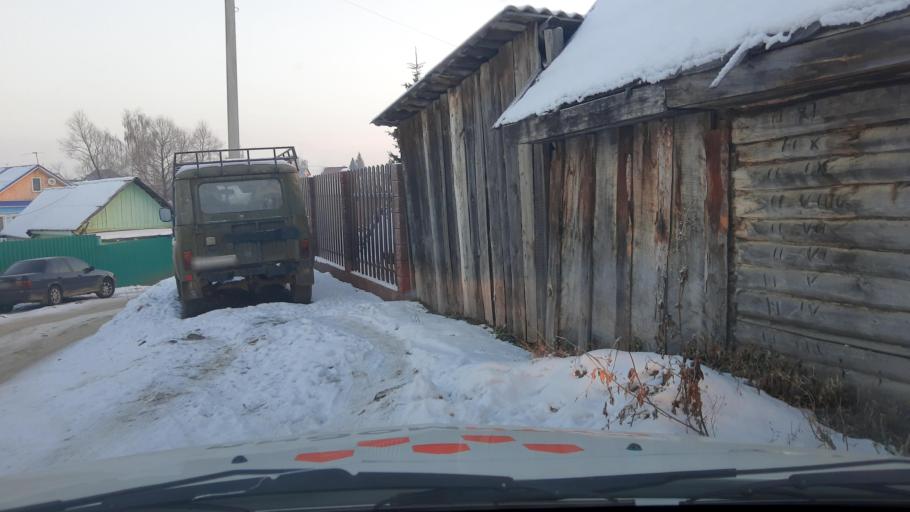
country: RU
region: Bashkortostan
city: Iglino
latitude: 54.8388
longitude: 56.4336
